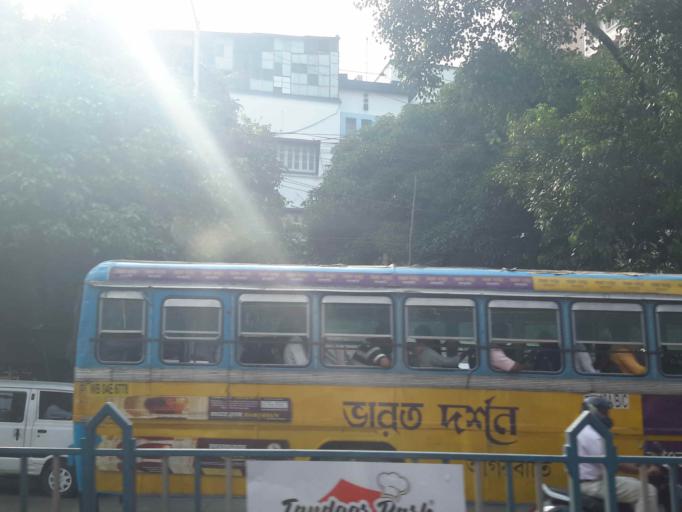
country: IN
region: West Bengal
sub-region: Kolkata
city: Kolkata
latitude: 22.5240
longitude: 88.3656
